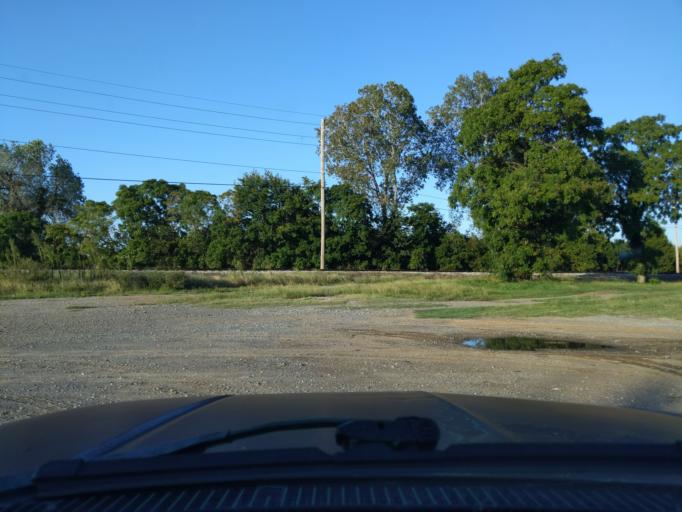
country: US
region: Oklahoma
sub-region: Tulsa County
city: Sand Springs
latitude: 36.1298
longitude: -96.1155
